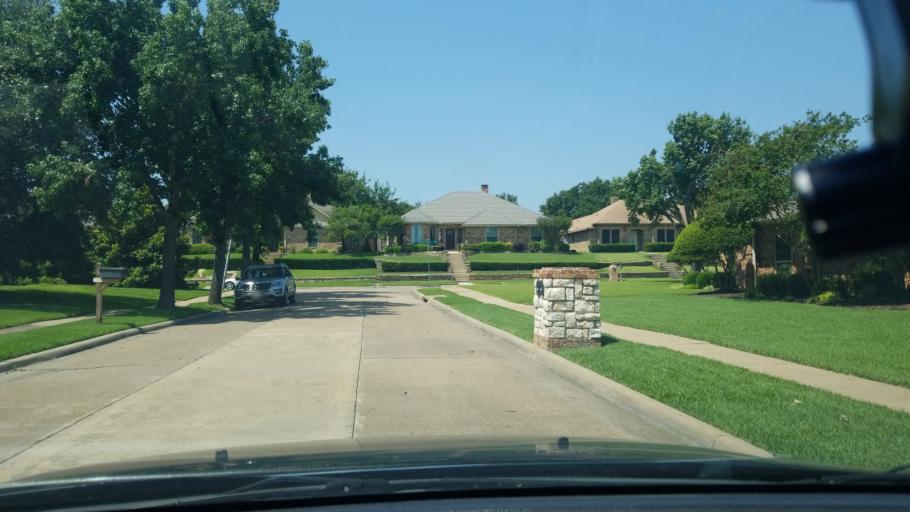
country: US
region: Texas
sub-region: Dallas County
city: Mesquite
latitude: 32.8269
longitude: -96.6161
